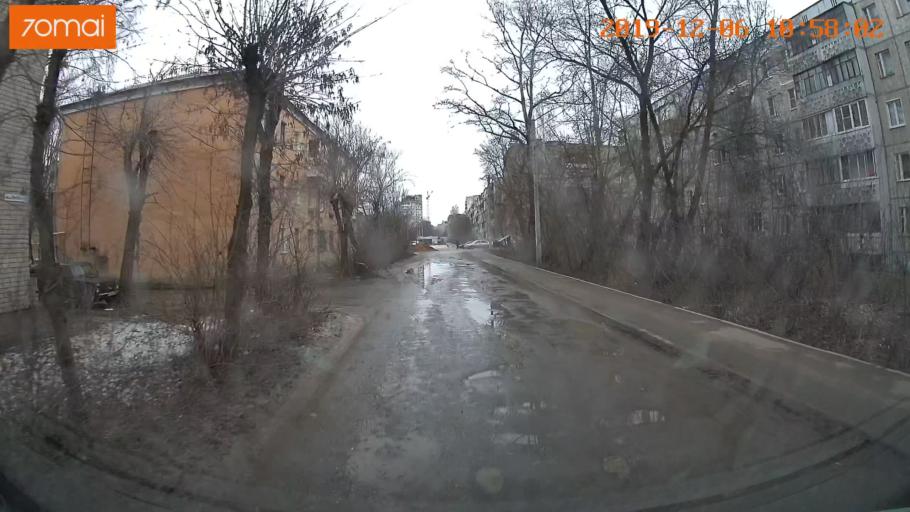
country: RU
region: Ivanovo
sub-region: Gorod Ivanovo
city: Ivanovo
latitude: 56.9687
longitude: 40.9779
